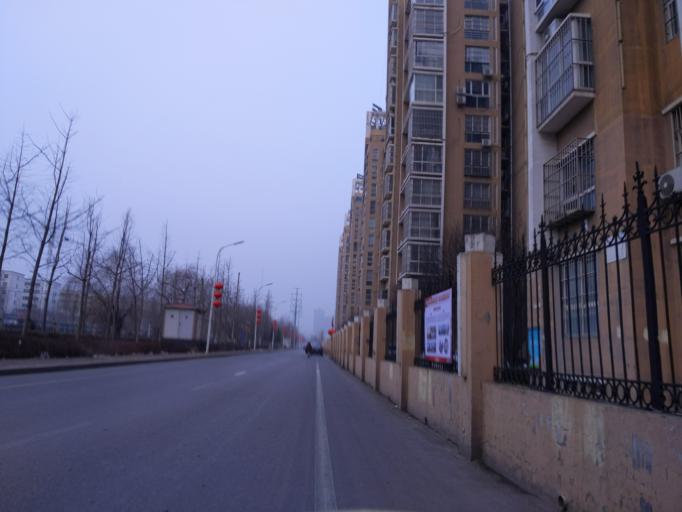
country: CN
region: Henan Sheng
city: Zhongyuanlu
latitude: 35.7661
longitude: 115.0477
